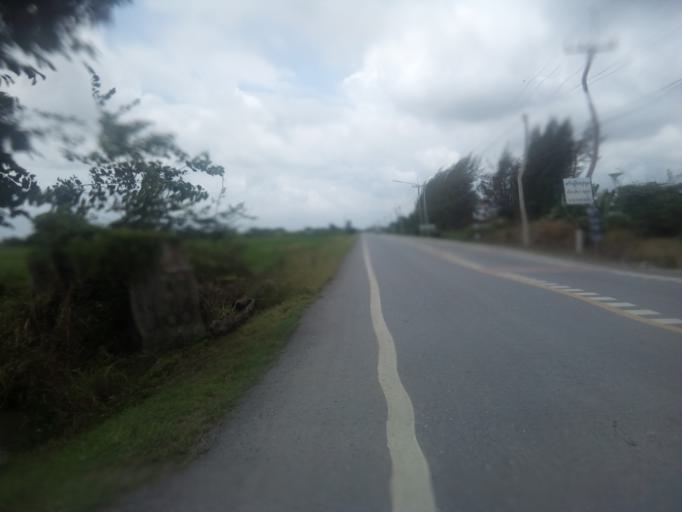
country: TH
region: Pathum Thani
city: Ban Lam Luk Ka
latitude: 14.0101
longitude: 100.8228
